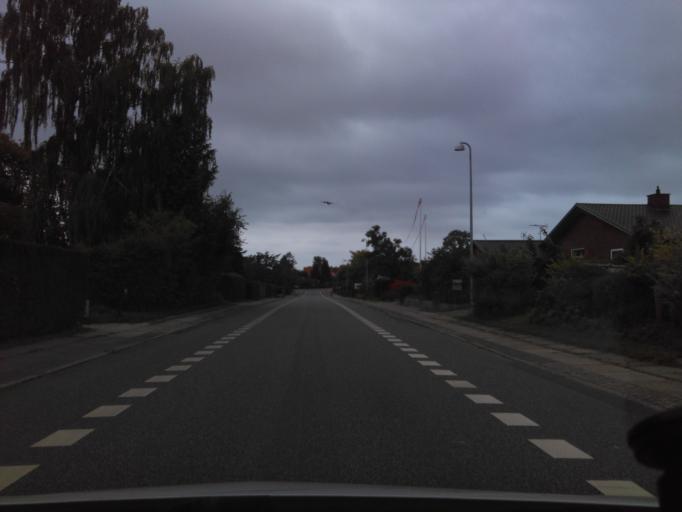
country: DK
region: Capital Region
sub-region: Fureso Kommune
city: Farum
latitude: 55.8117
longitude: 12.3466
